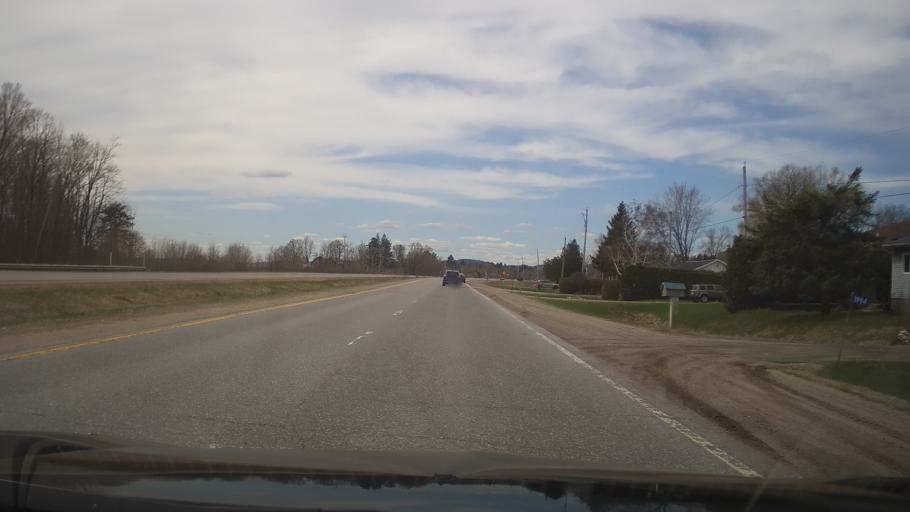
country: CA
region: Quebec
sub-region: Outaouais
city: Wakefield
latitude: 45.5261
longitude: -75.9975
